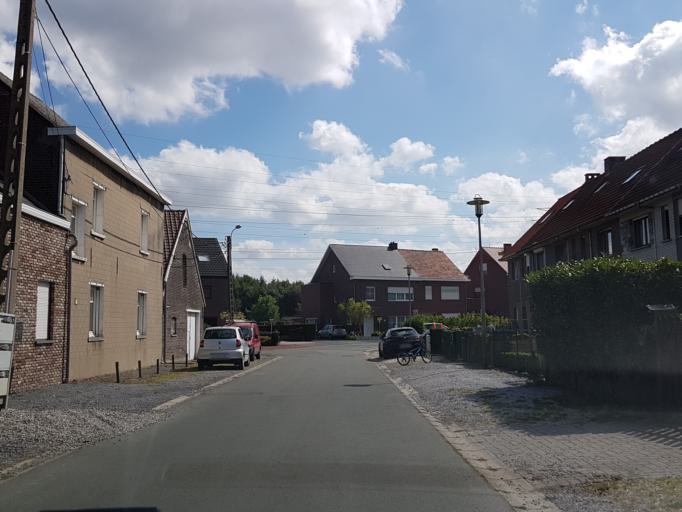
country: BE
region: Flanders
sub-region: Provincie Vlaams-Brabant
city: Vilvoorde
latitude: 50.9525
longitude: 4.4204
